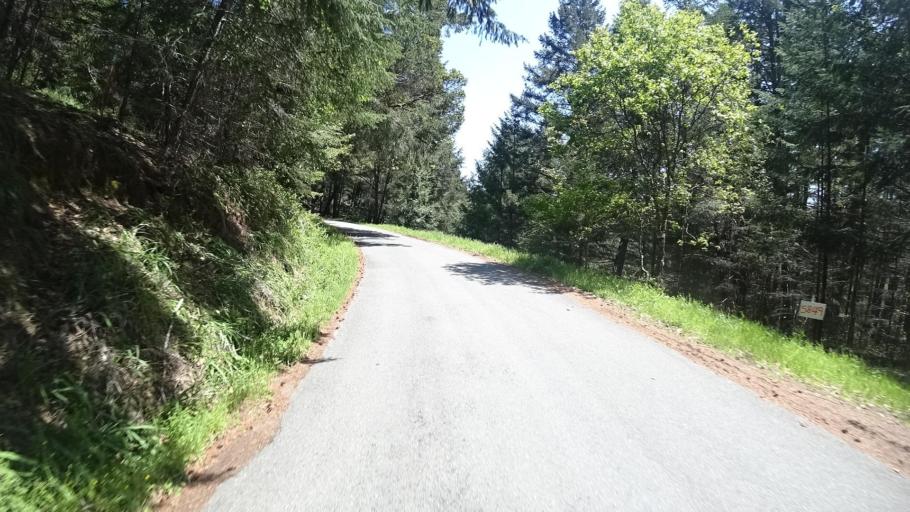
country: US
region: California
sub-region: Humboldt County
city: Redway
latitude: 40.1904
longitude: -123.5340
